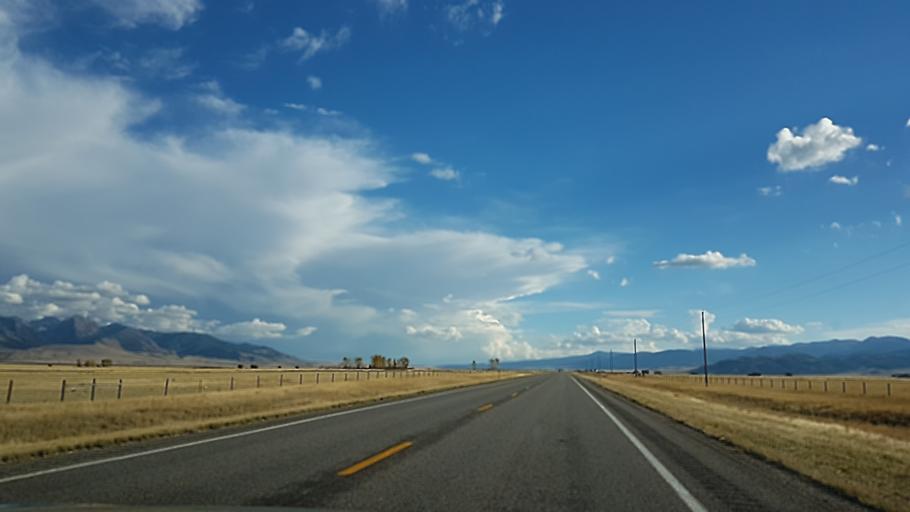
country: US
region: Montana
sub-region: Madison County
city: Virginia City
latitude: 45.1919
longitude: -111.6789
